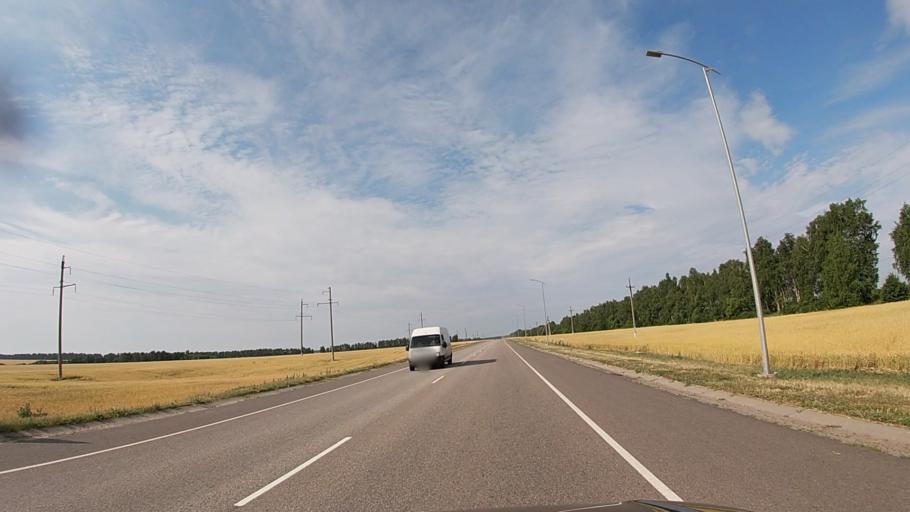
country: RU
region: Belgorod
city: Proletarskiy
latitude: 50.8285
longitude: 35.7625
